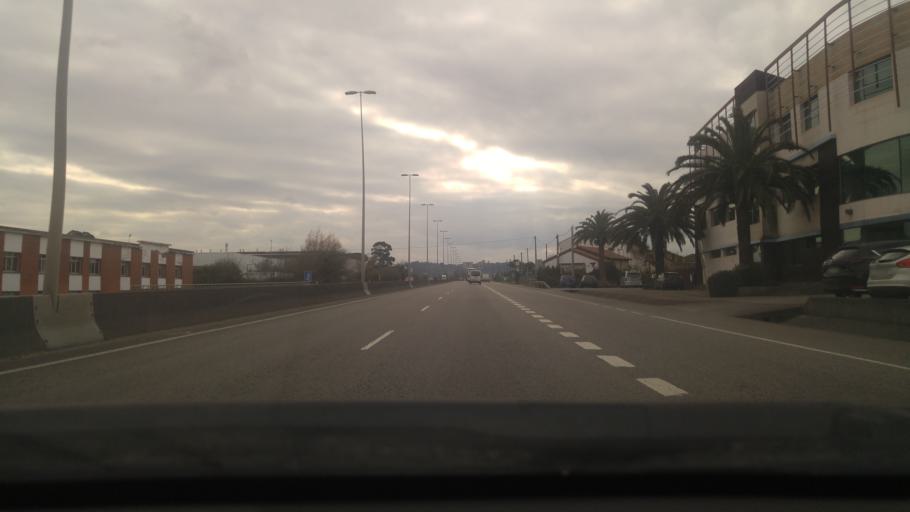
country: ES
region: Asturias
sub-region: Province of Asturias
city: Natahoyo
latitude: 43.5043
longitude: -5.7000
